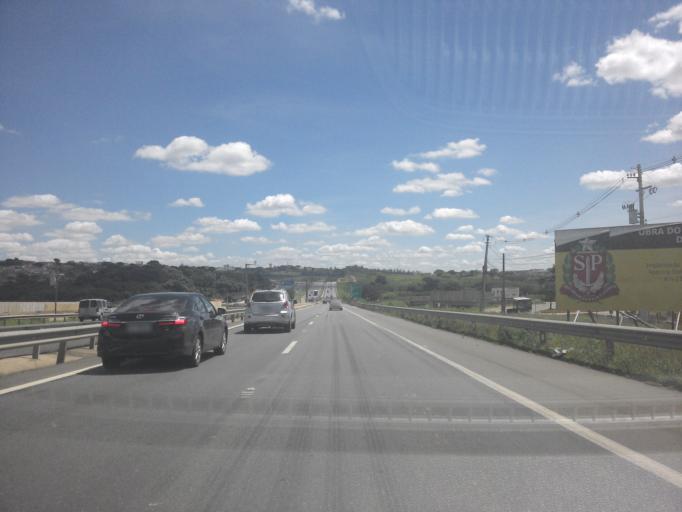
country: BR
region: Sao Paulo
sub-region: Campinas
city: Campinas
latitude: -22.8503
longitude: -47.0278
